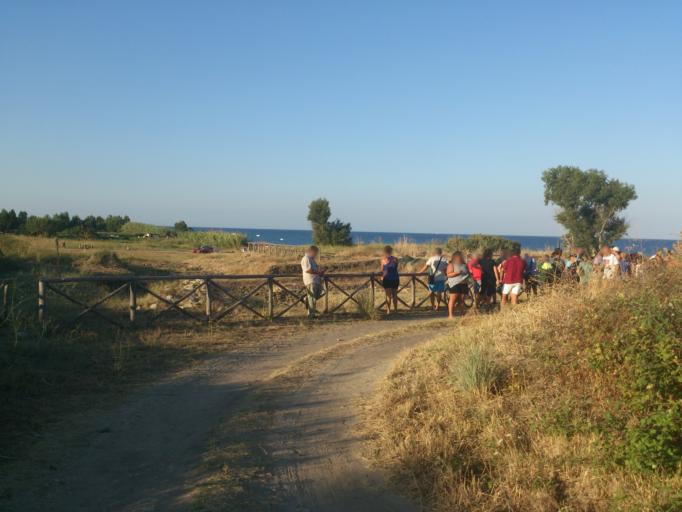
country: IT
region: Calabria
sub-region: Provincia di Reggio Calabria
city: Monasterace Marina
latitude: 38.4486
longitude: 16.5795
